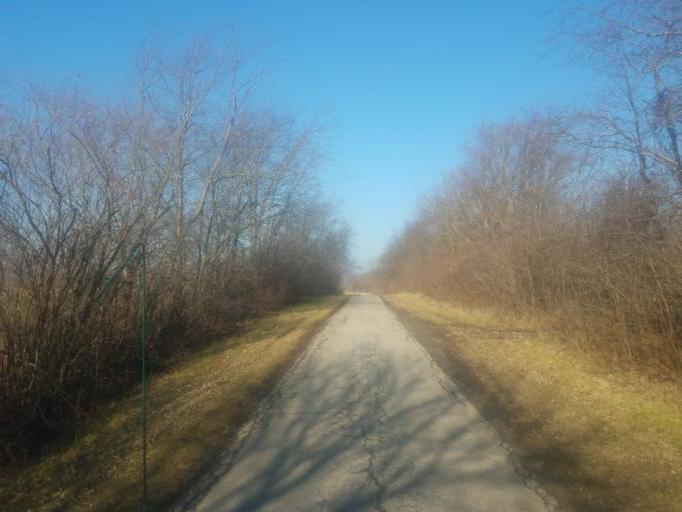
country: US
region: Ohio
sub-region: Seneca County
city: Tiffin
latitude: 41.0583
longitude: -83.0175
